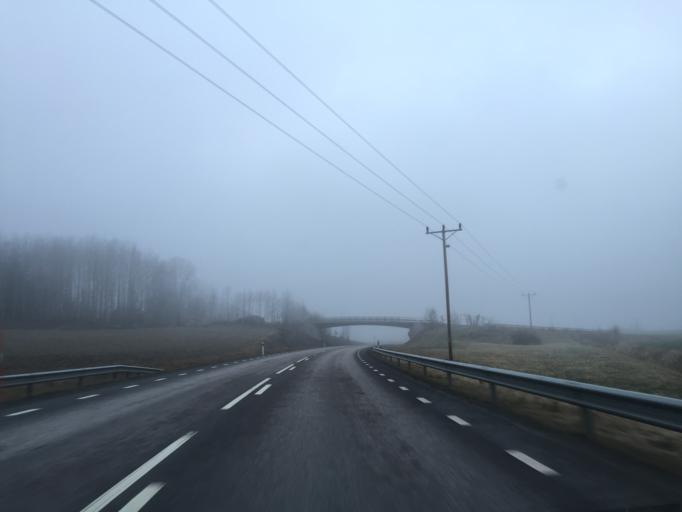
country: SE
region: Soedermanland
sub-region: Nykopings Kommun
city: Olstorp
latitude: 58.8962
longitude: 16.6452
